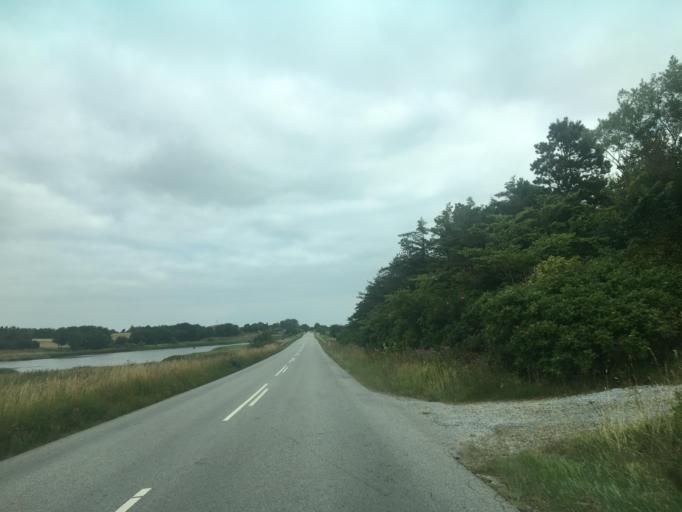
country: DK
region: North Denmark
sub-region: Thisted Kommune
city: Thisted
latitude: 56.8696
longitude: 8.6217
